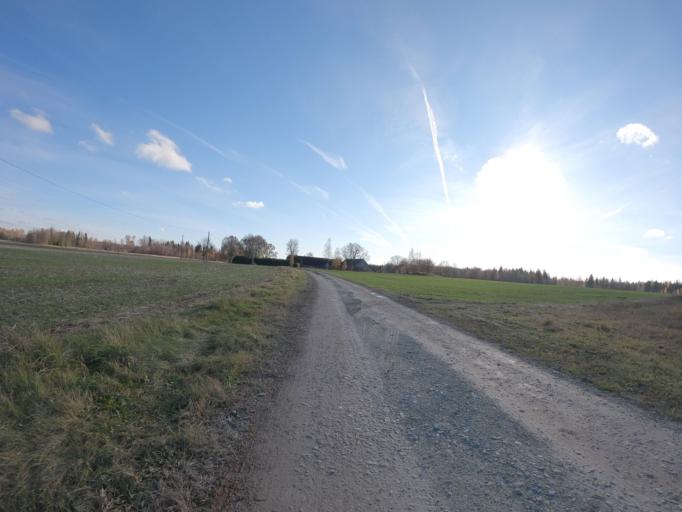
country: EE
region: Raplamaa
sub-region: Rapla vald
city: Rapla
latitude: 59.0266
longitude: 24.7943
